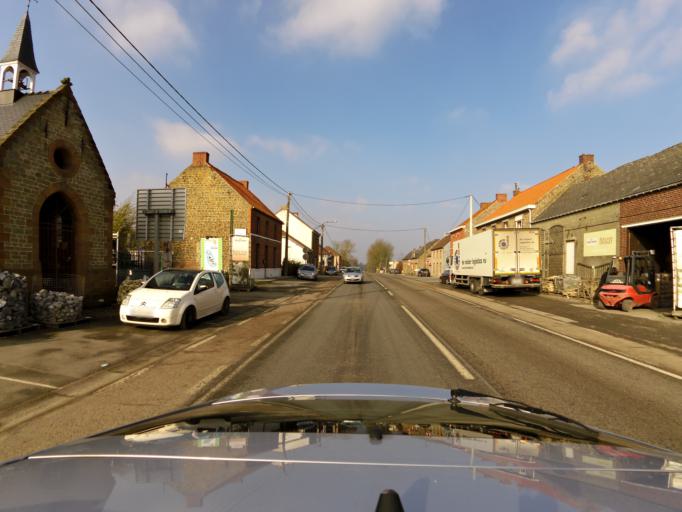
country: BE
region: Wallonia
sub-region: Province du Hainaut
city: Beloeil
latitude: 50.4989
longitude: 3.7082
